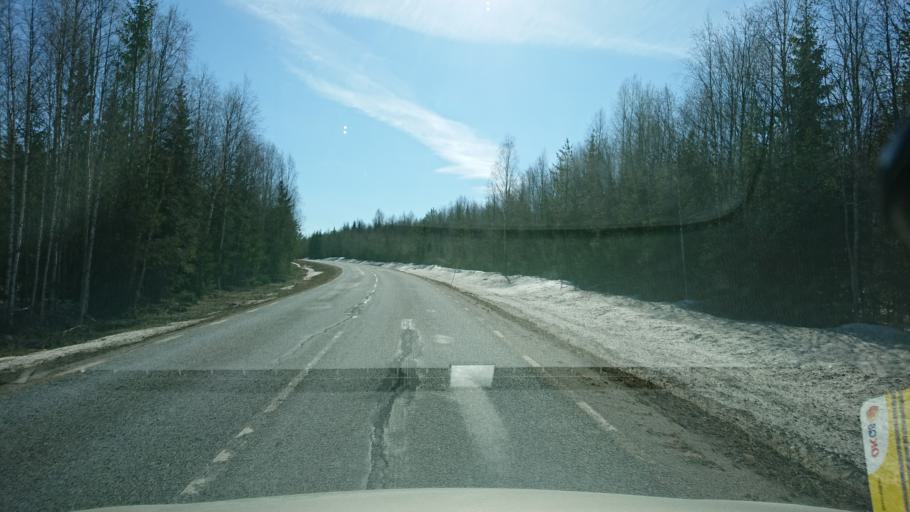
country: SE
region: Vaesterbotten
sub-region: Dorotea Kommun
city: Dorotea
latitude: 63.9972
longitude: 16.3066
